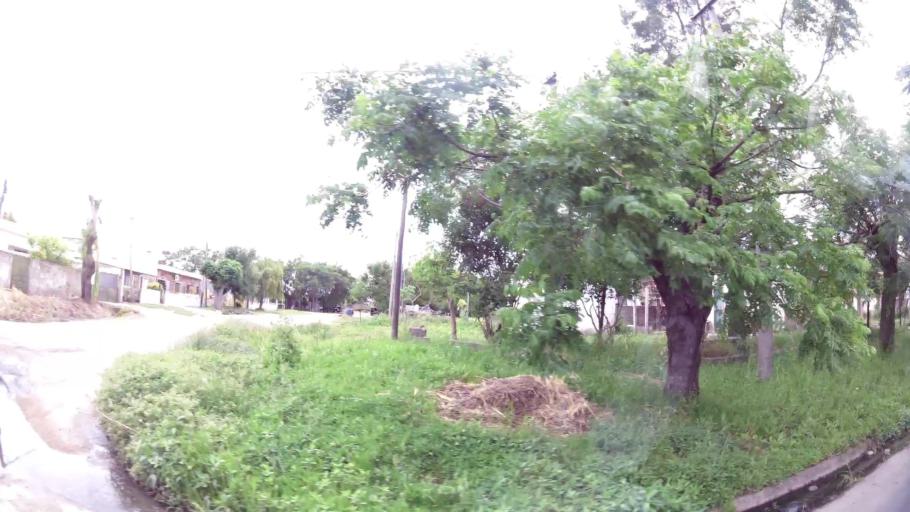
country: UY
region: Canelones
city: La Paz
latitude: -34.7519
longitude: -56.2277
